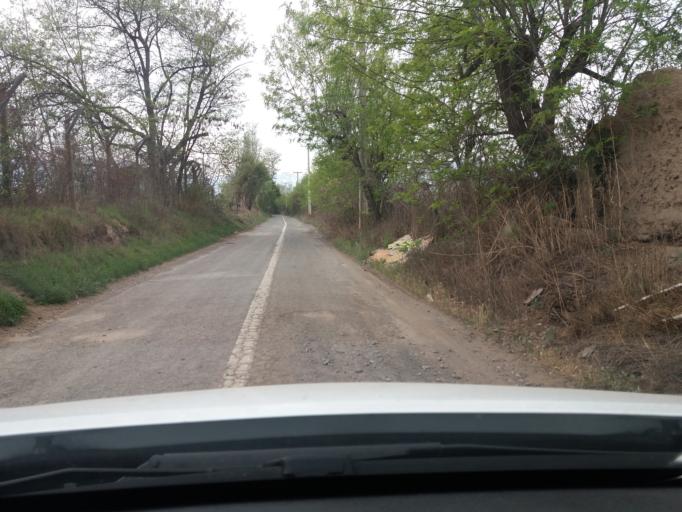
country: CL
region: Valparaiso
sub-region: Provincia de Los Andes
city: Los Andes
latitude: -32.8249
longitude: -70.6403
